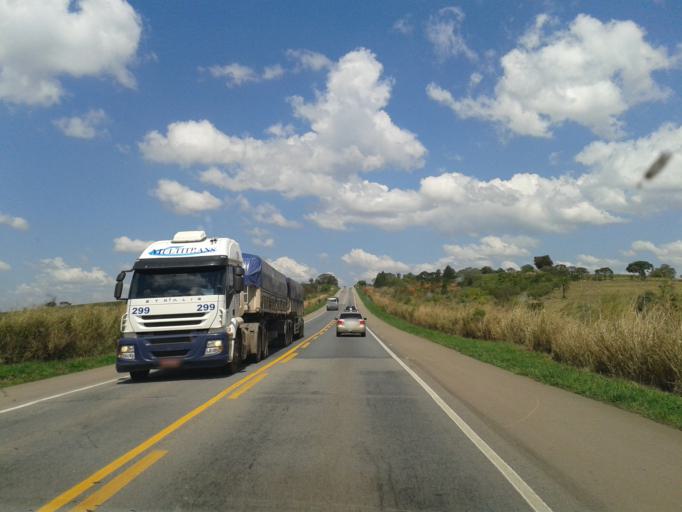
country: BR
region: Minas Gerais
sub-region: Campos Altos
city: Campos Altos
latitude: -19.6921
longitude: -46.0370
